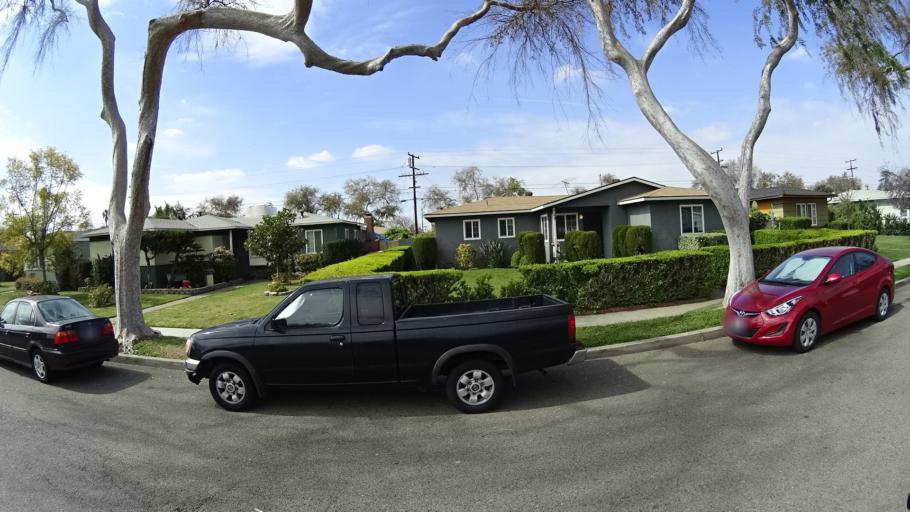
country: US
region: California
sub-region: Orange County
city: Anaheim
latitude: 33.8252
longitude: -117.9216
